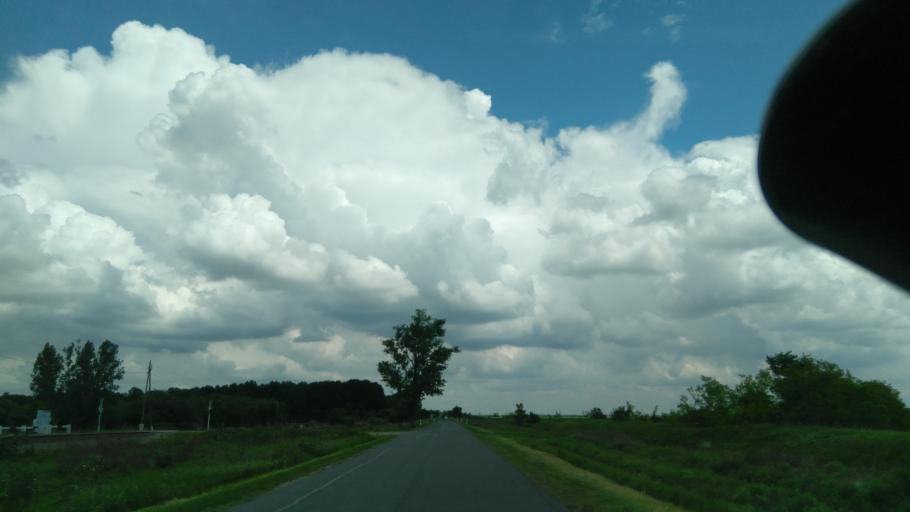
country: HU
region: Bekes
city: Devavanya
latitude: 46.9901
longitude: 20.8992
